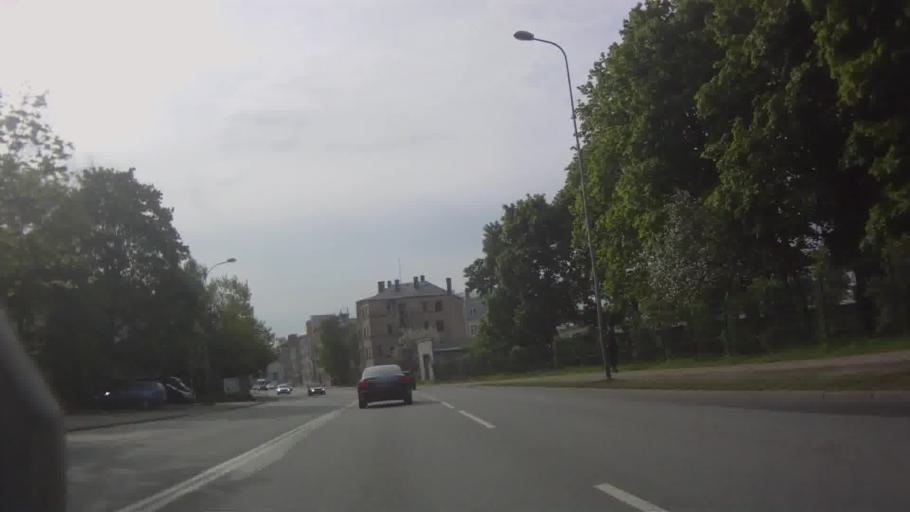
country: LV
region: Riga
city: Riga
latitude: 56.9688
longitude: 24.1426
